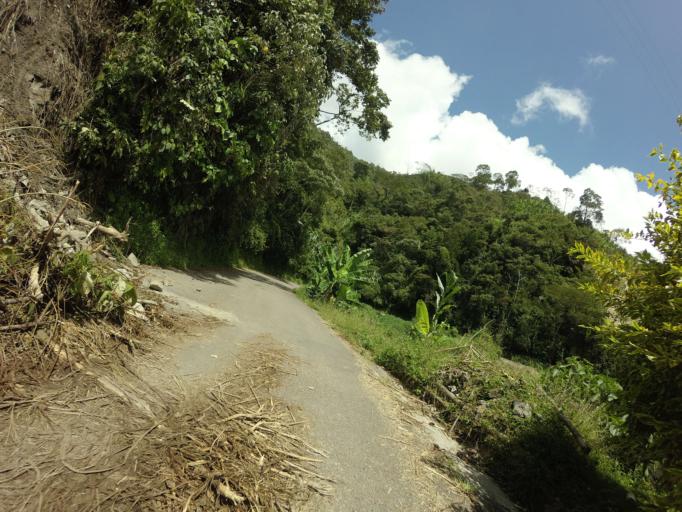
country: CO
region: Caldas
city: Marquetalia
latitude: 5.2916
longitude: -75.1001
